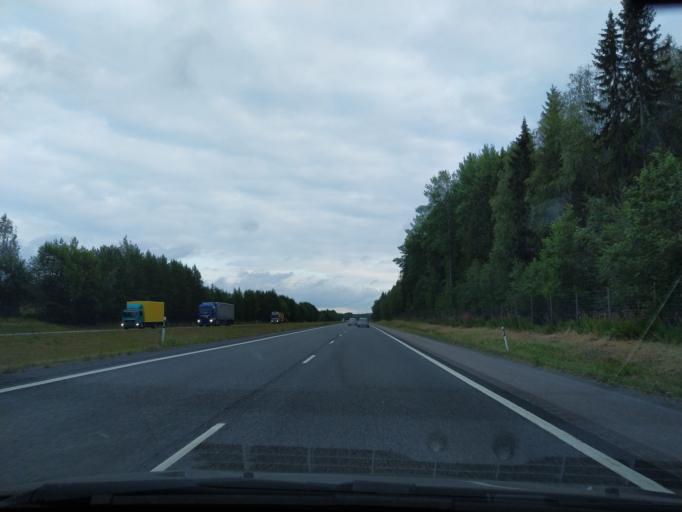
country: FI
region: Haeme
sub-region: Haemeenlinna
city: Tervakoski
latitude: 60.7905
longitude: 24.6961
